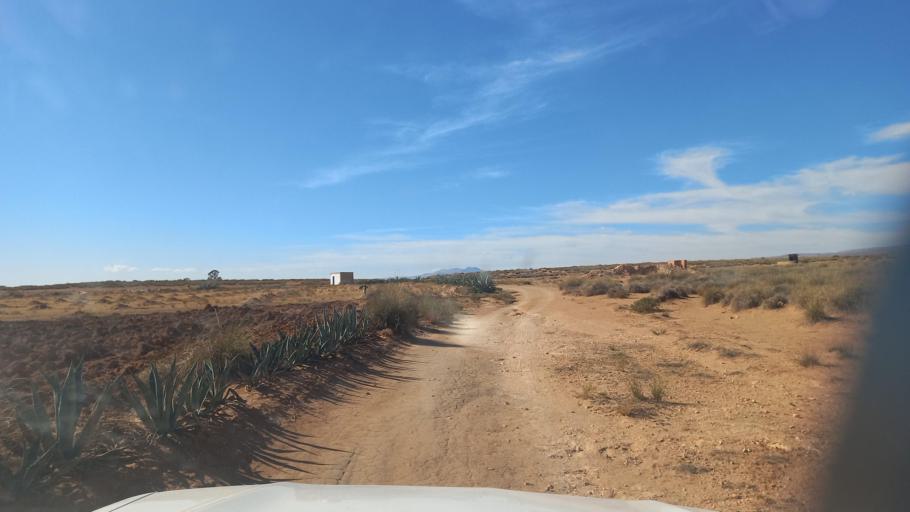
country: TN
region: Al Qasrayn
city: Kasserine
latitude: 35.2146
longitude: 8.9785
